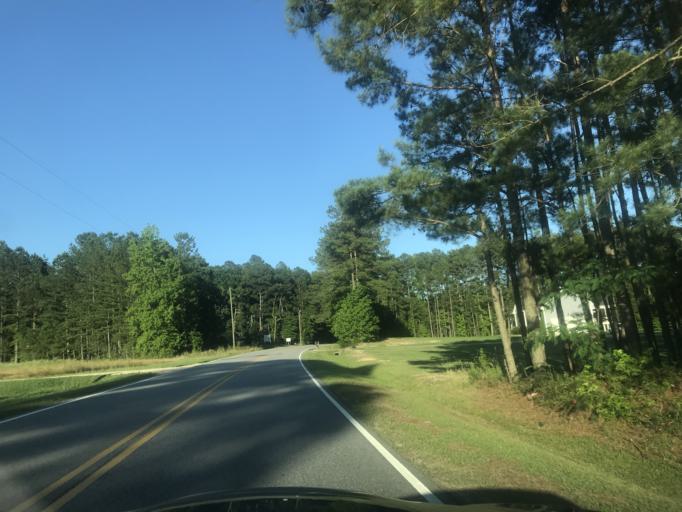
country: US
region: North Carolina
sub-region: Johnston County
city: Archer Lodge
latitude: 35.7313
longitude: -78.3992
